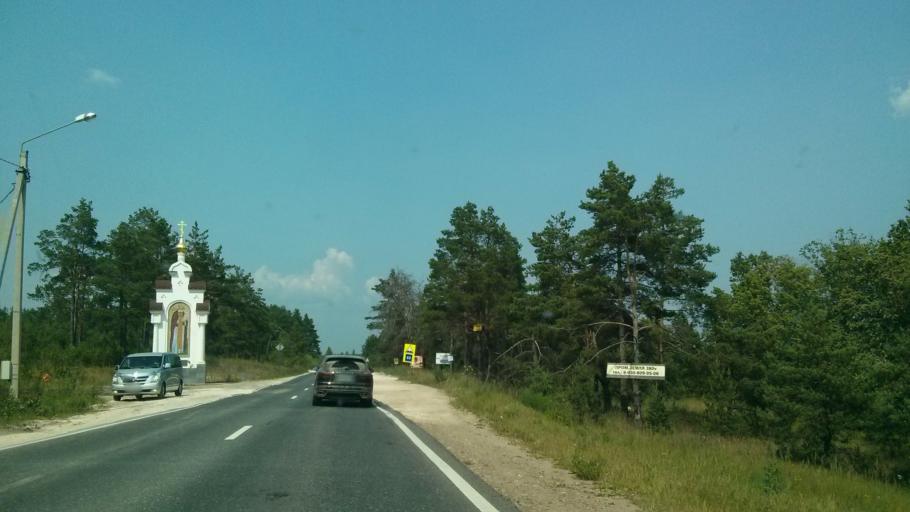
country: RU
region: Nizjnij Novgorod
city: Navashino
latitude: 55.5881
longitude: 42.1505
